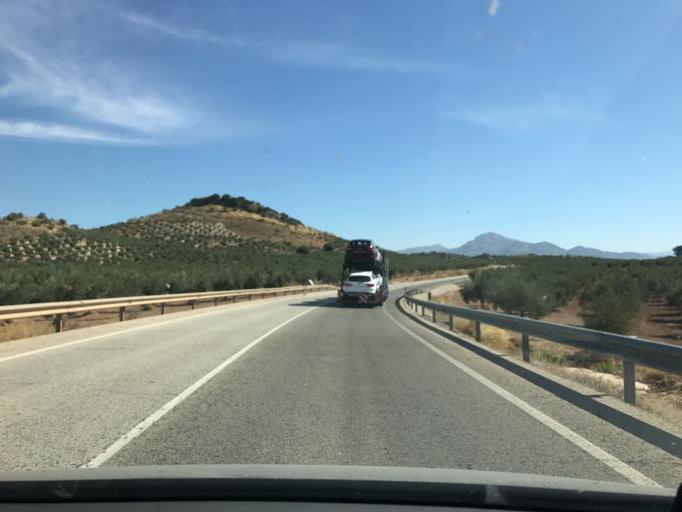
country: ES
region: Andalusia
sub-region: Province of Cordoba
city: Fuente-Tojar
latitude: 37.5627
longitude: -4.1906
